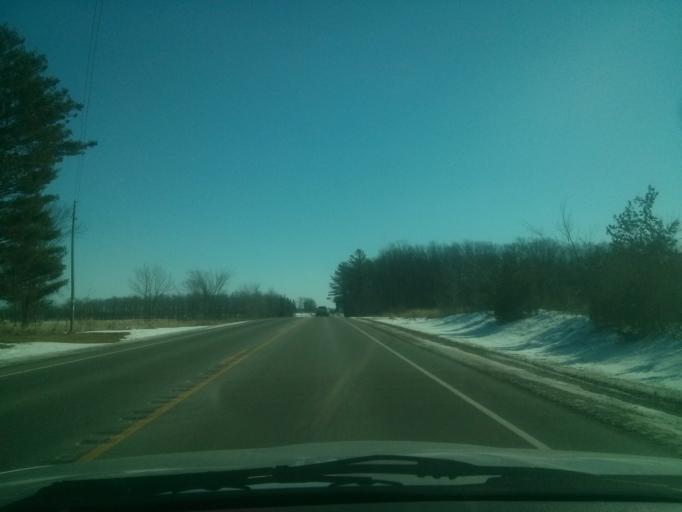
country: US
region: Wisconsin
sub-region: Polk County
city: Clear Lake
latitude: 45.1365
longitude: -92.2892
